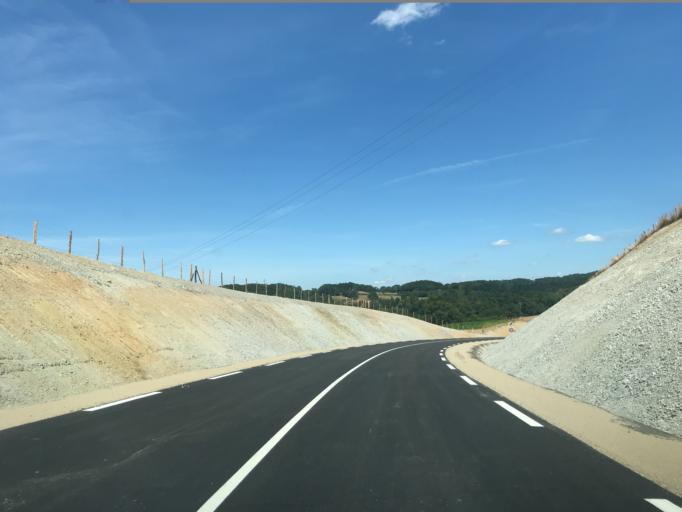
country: FR
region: Limousin
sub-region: Departement de la Creuse
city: Aubusson
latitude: 45.9449
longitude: 2.1929
